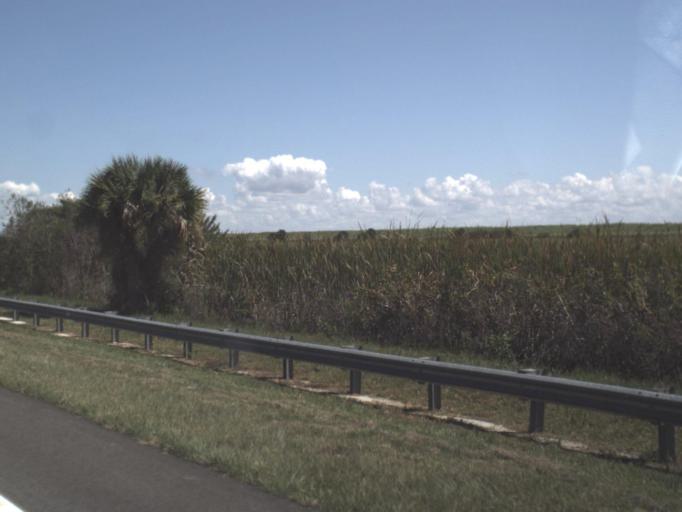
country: US
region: Florida
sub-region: Glades County
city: Buckhead Ridge
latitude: 27.0382
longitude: -80.9970
